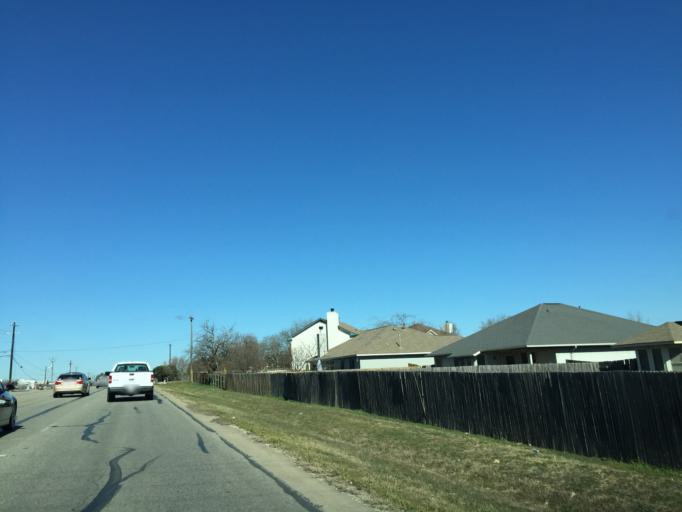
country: US
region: Texas
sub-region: Williamson County
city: Leander
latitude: 30.5619
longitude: -97.8626
